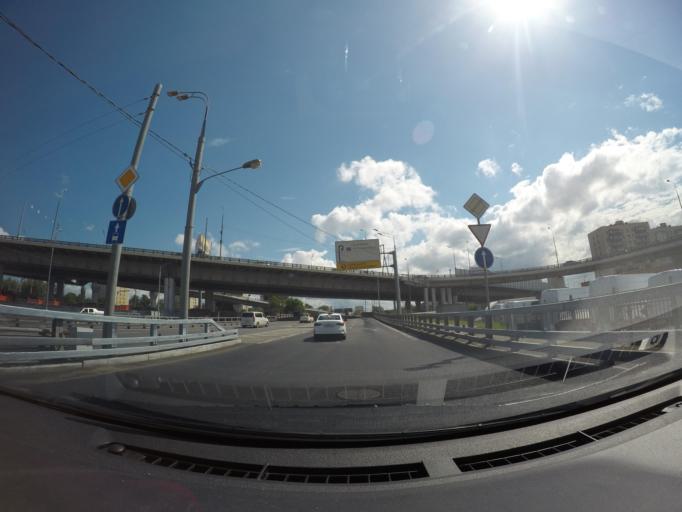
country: RU
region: Moscow
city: Lefortovo
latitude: 55.7364
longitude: 37.6973
